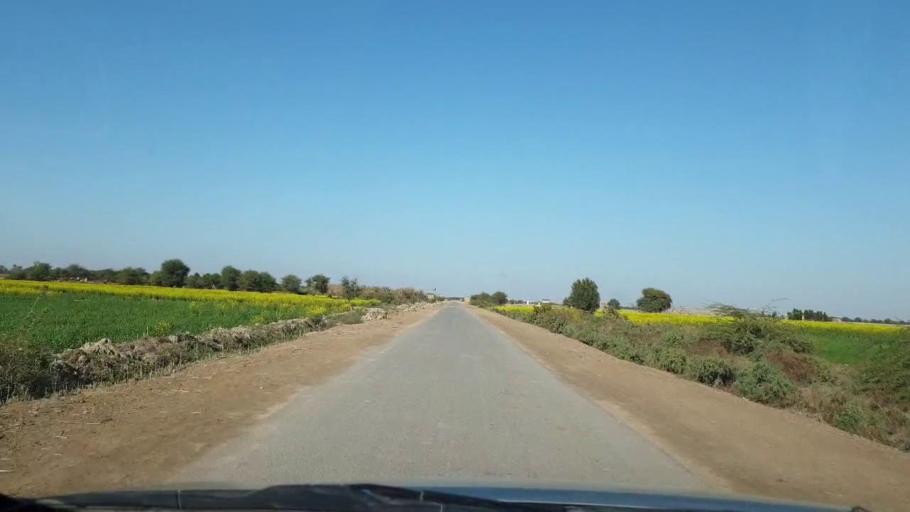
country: PK
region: Sindh
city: Jhol
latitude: 25.8298
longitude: 68.9501
